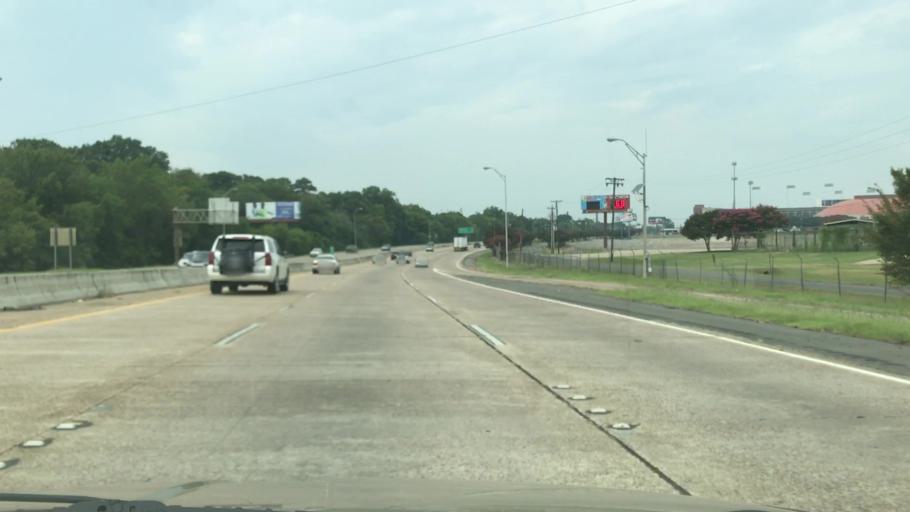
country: US
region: Louisiana
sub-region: Caddo Parish
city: Shreveport
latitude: 32.4781
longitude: -93.7811
